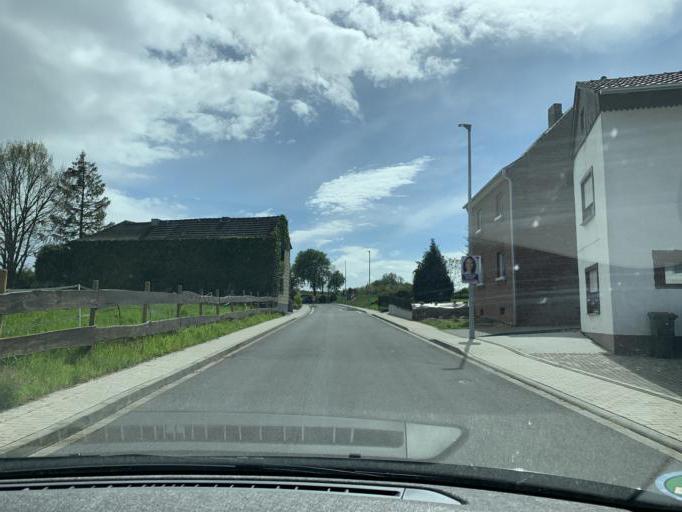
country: DE
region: North Rhine-Westphalia
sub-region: Regierungsbezirk Koln
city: Bad Munstereifel
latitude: 50.6078
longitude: 6.7216
